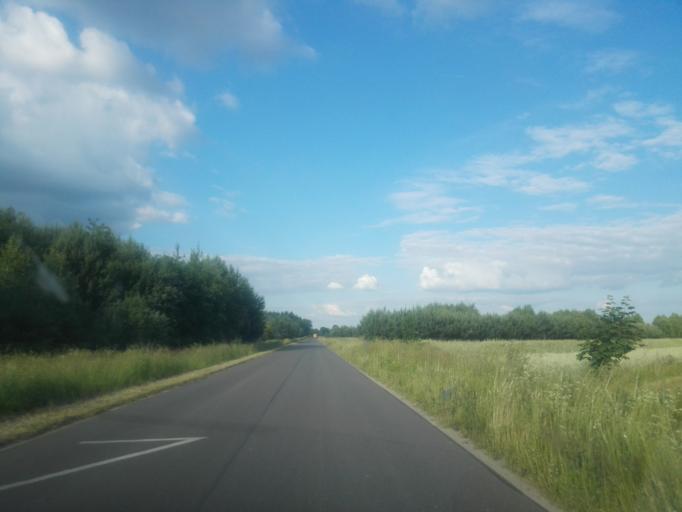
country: PL
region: Swietokrzyskie
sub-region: Powiat jedrzejowski
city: Slupia
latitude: 50.7076
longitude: 19.9564
